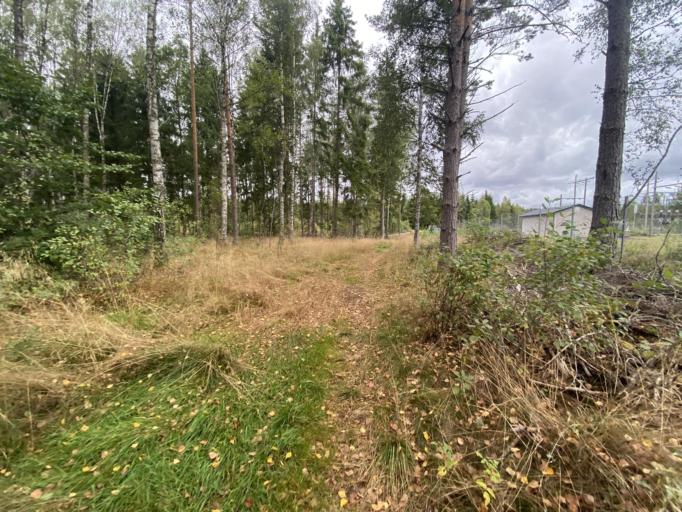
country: SE
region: Kronoberg
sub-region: Markaryds Kommun
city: Markaryd
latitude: 56.4862
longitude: 13.5987
